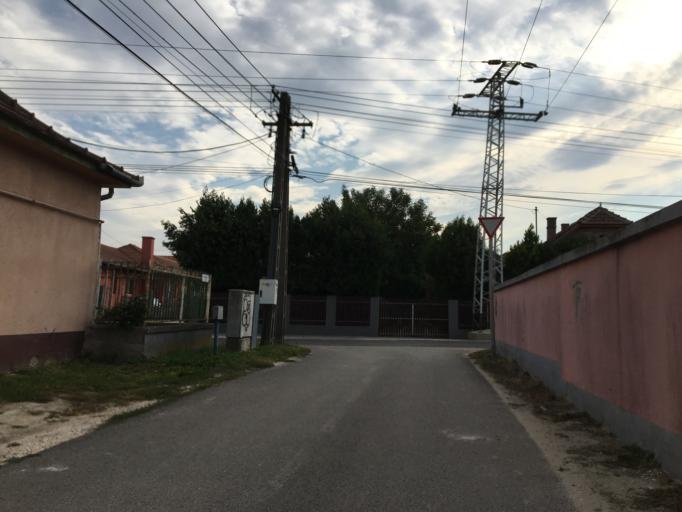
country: HU
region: Pest
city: Szigetszentmiklos
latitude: 47.3512
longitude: 19.0317
